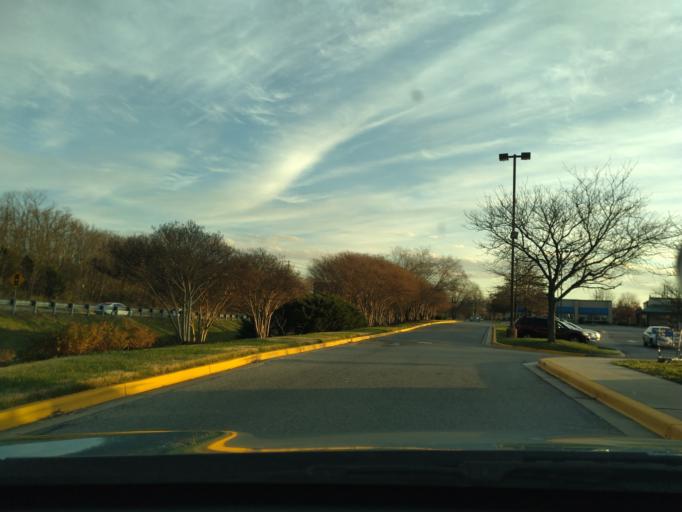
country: US
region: Maryland
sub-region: Prince George's County
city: Clinton
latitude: 38.7702
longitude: -76.8866
